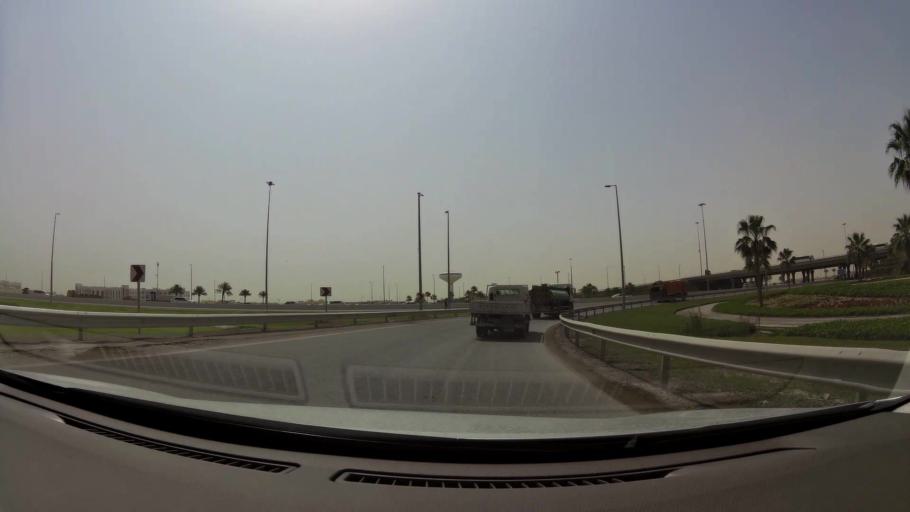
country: QA
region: Baladiyat ar Rayyan
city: Ar Rayyan
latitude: 25.2124
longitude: 51.4075
